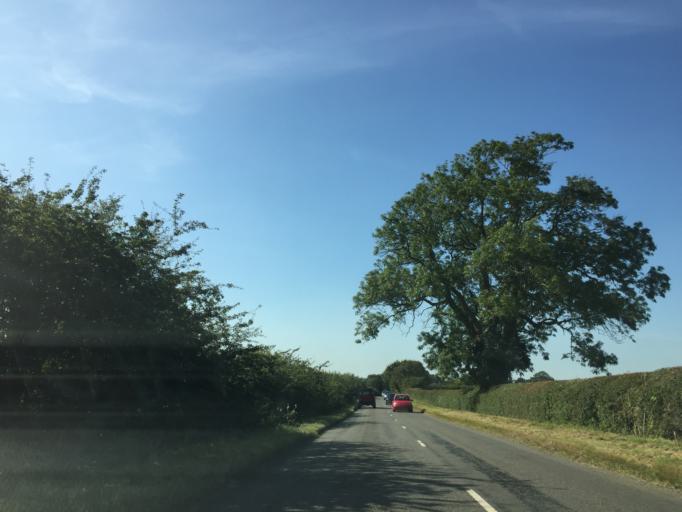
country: GB
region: England
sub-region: Leicestershire
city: Queniborough
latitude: 52.7008
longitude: -1.0254
